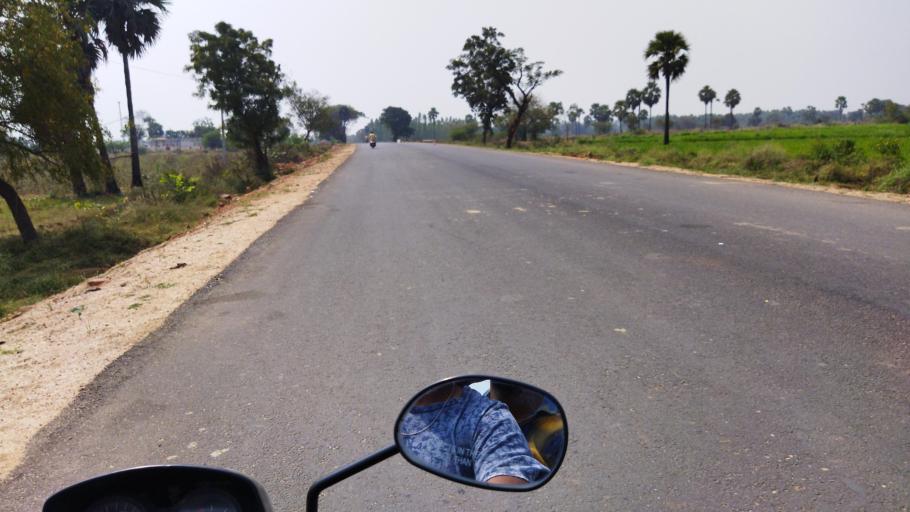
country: IN
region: Telangana
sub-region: Nalgonda
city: Nalgonda
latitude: 17.1553
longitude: 79.4114
